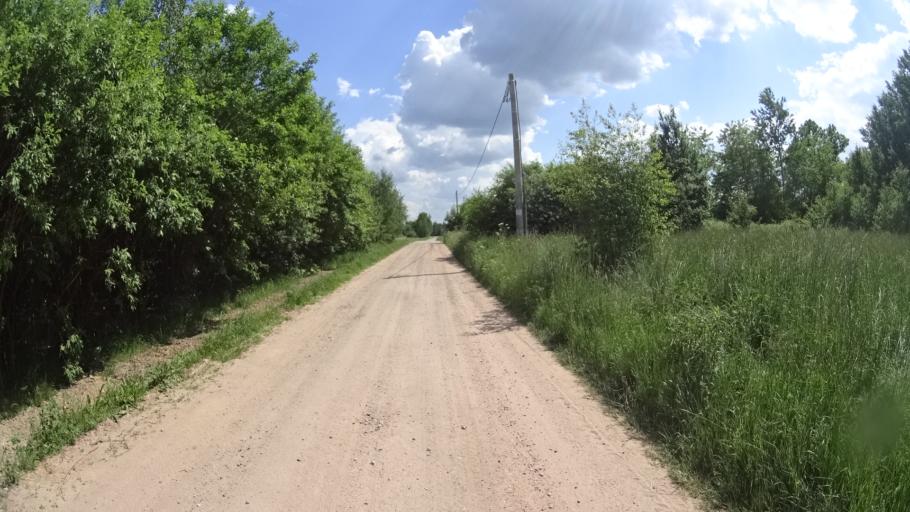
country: PL
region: Masovian Voivodeship
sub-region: Powiat piaseczynski
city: Tarczyn
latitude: 52.0186
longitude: 20.8173
